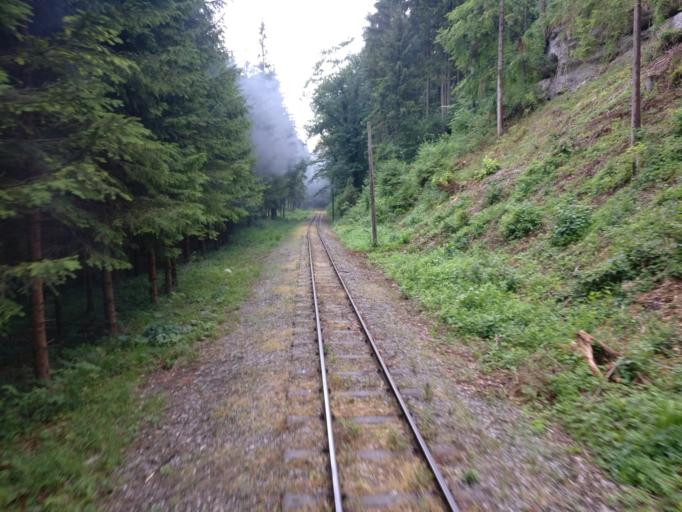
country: AT
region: Upper Austria
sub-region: Politischer Bezirk Steyr-Land
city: Waldneukirchen
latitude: 47.9990
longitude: 14.2839
